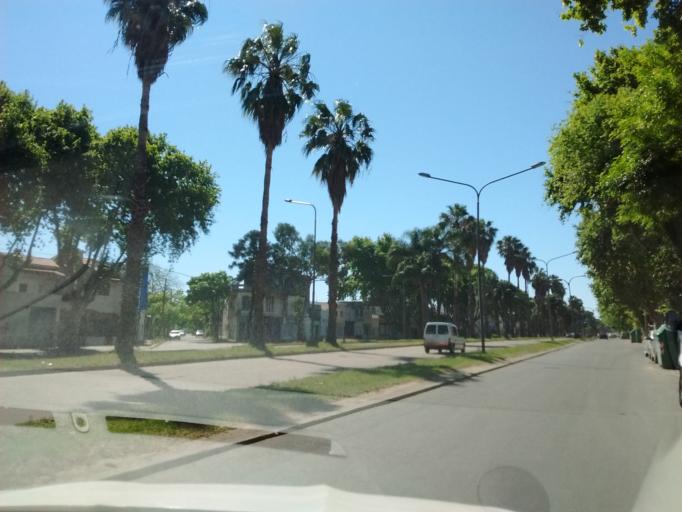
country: AR
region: Santa Fe
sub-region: Departamento de Rosario
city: Rosario
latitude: -32.9115
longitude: -60.6871
